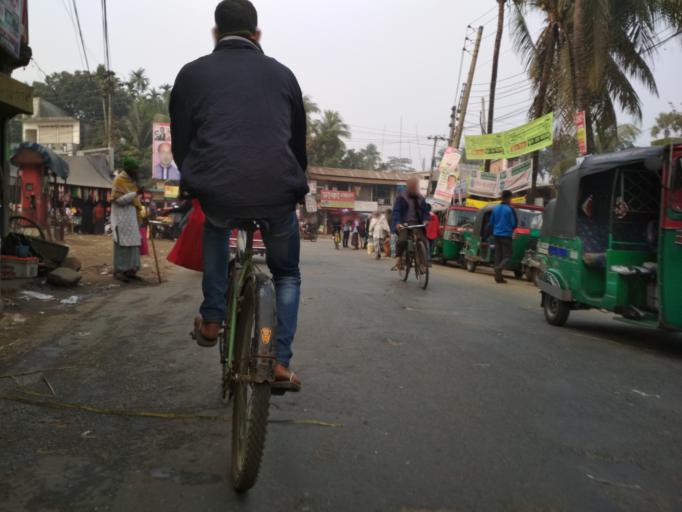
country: BD
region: Chittagong
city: Lakshmipur
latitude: 22.9323
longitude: 90.8333
